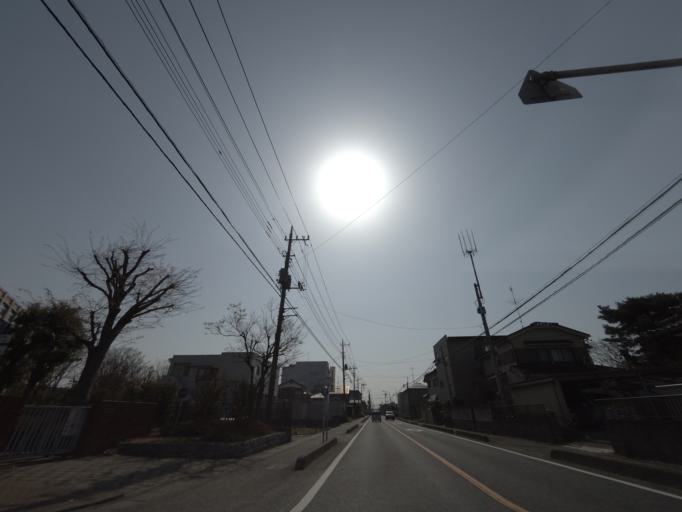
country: JP
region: Saitama
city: Yono
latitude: 35.8878
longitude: 139.5889
